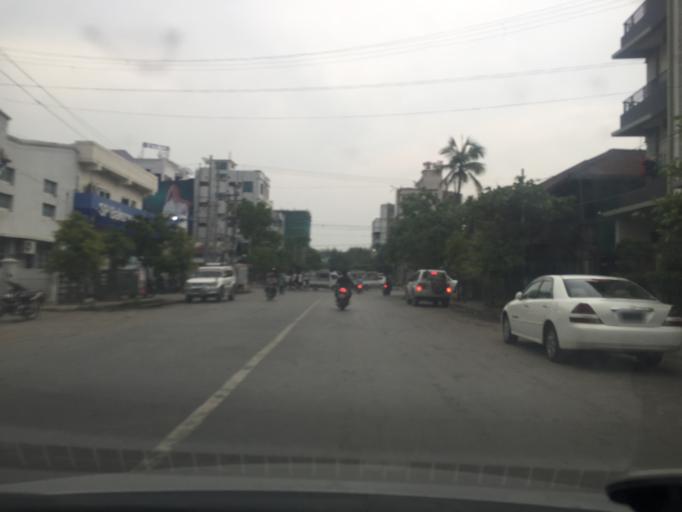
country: MM
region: Mandalay
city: Mandalay
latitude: 21.9740
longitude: 96.0833
